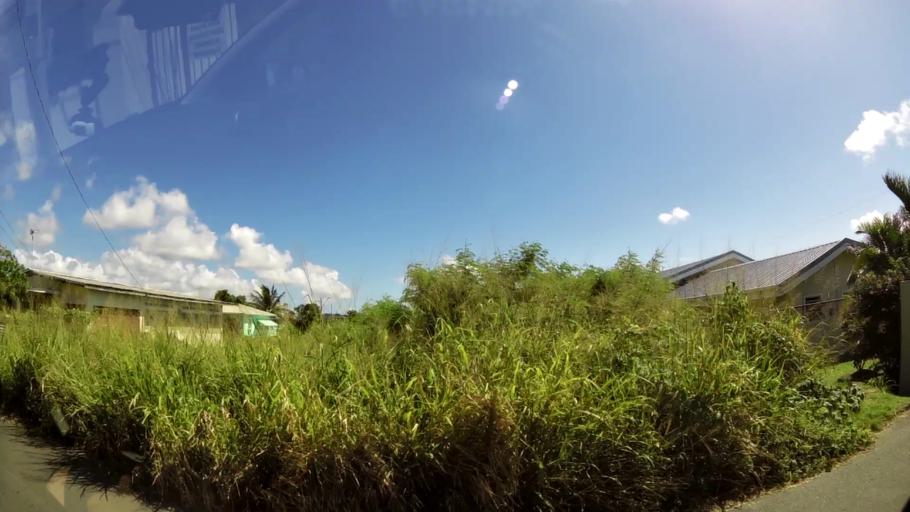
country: TT
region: Tobago
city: Scarborough
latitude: 11.1691
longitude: -60.7586
